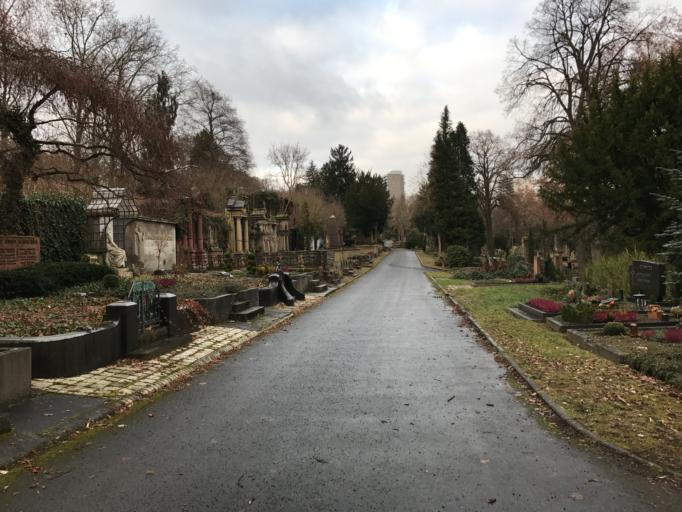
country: DE
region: Rheinland-Pfalz
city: Mainz
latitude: 49.9935
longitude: 8.2488
